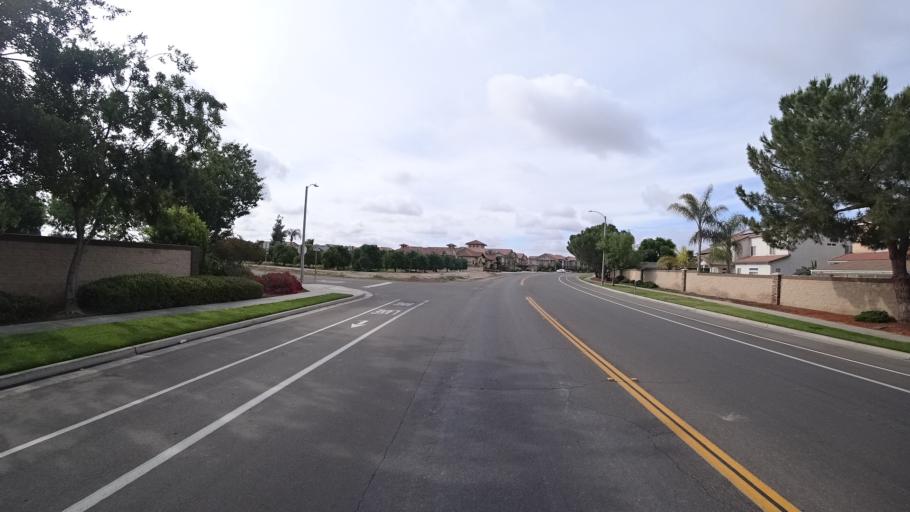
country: US
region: California
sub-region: Kings County
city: Hanford
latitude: 36.3329
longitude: -119.6788
